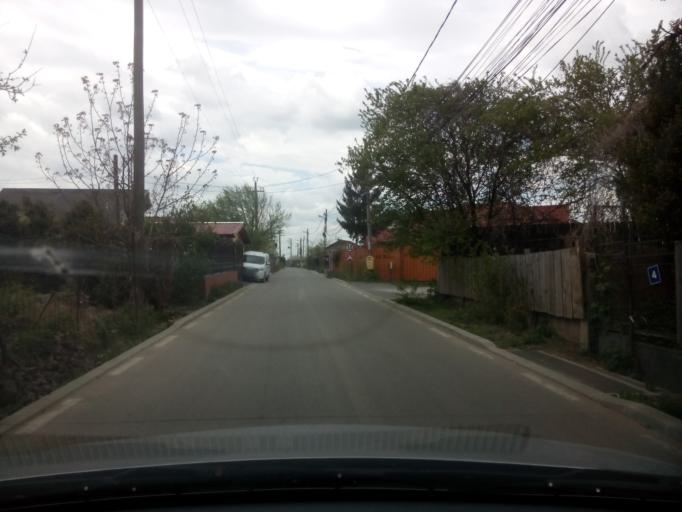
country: RO
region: Ilfov
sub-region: Comuna Otopeni
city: Otopeni
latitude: 44.5527
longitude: 26.0673
